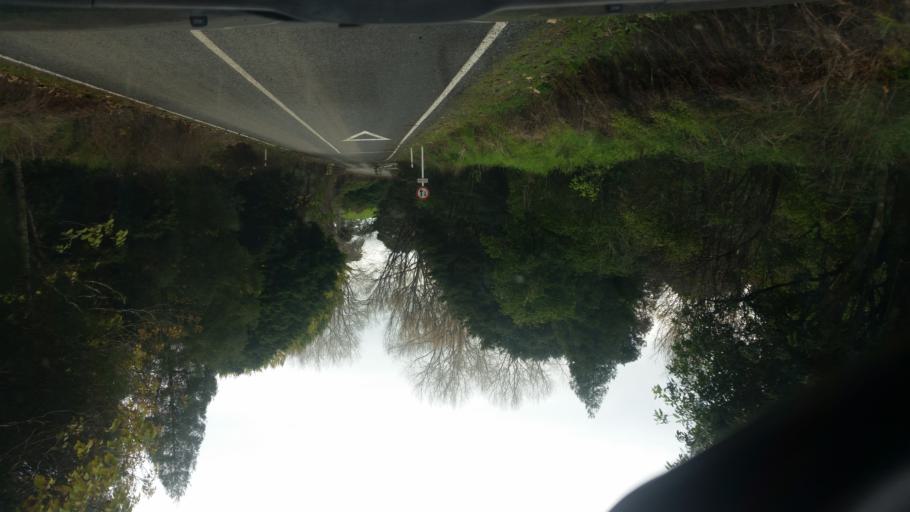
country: NZ
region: Northland
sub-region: Kaipara District
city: Dargaville
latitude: -35.7507
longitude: 173.9040
